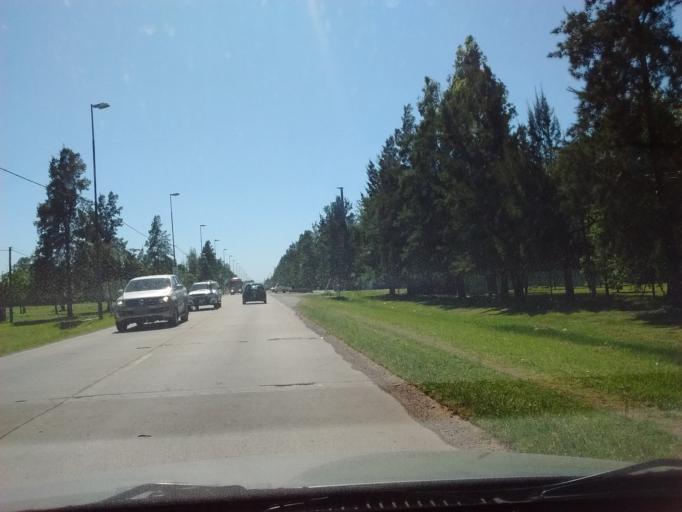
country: AR
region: Santa Fe
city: Funes
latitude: -32.9092
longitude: -60.7611
